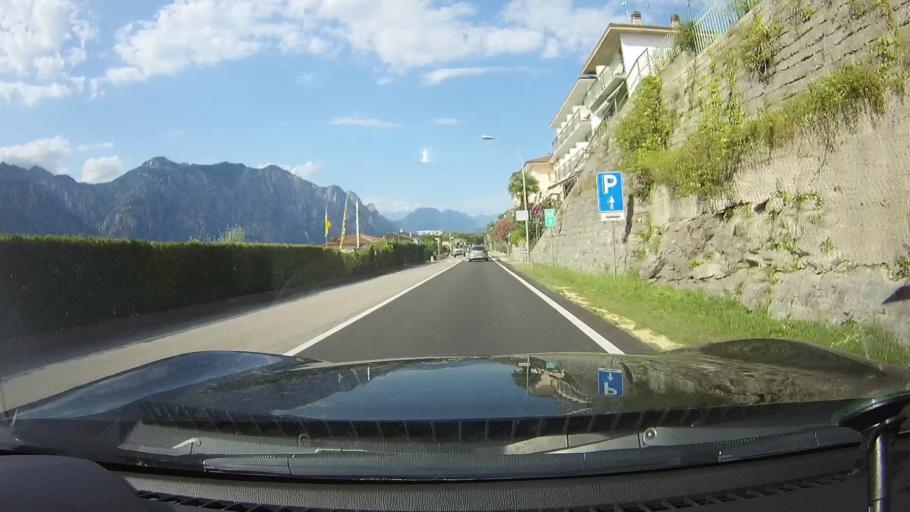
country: IT
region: Veneto
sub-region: Provincia di Verona
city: Malcesine
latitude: 45.7717
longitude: 10.8125
